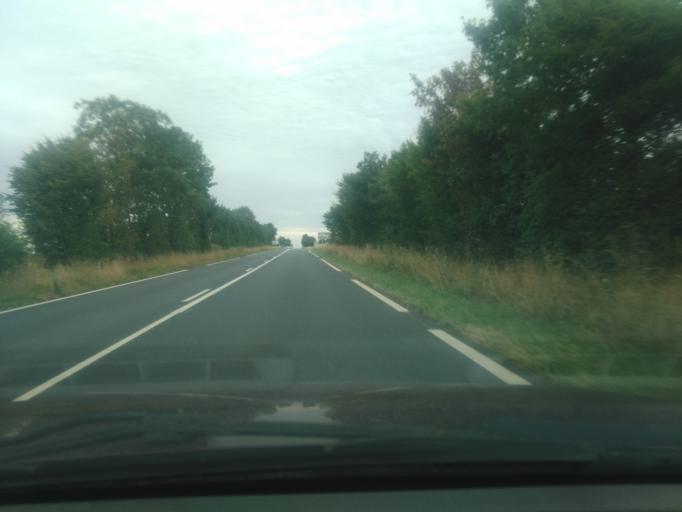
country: FR
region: Centre
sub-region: Departement de l'Indre
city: Le Pechereau
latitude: 46.6022
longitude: 1.6205
